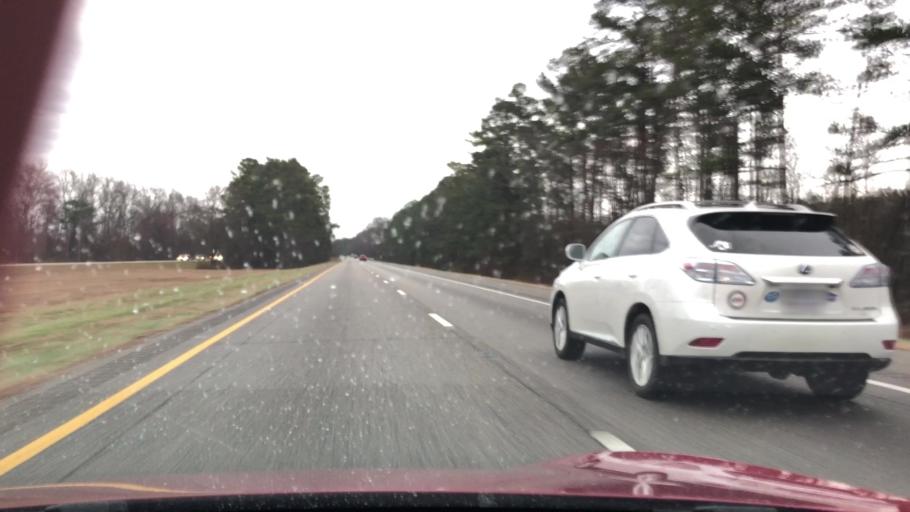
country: US
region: South Carolina
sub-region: Dillon County
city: Latta
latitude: 34.3544
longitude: -79.5158
